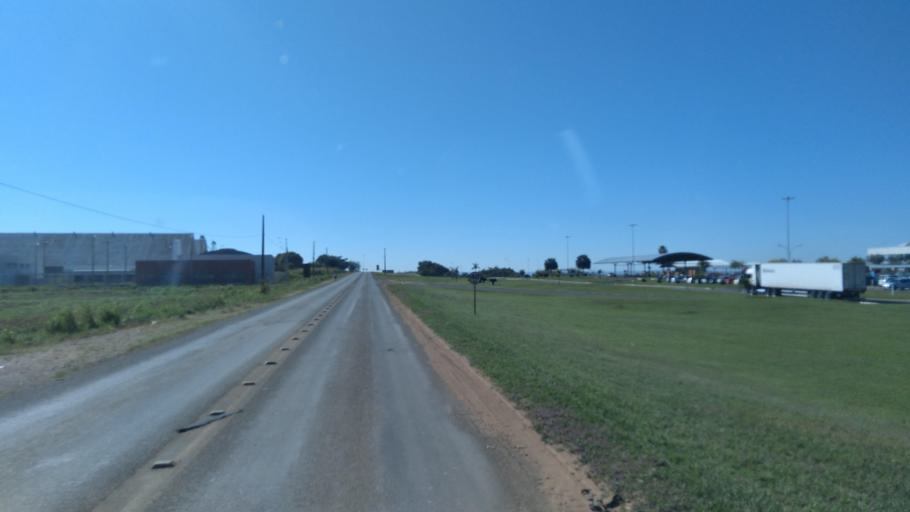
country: BR
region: Goias
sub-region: Mineiros
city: Mineiros
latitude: -17.5796
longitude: -52.5404
